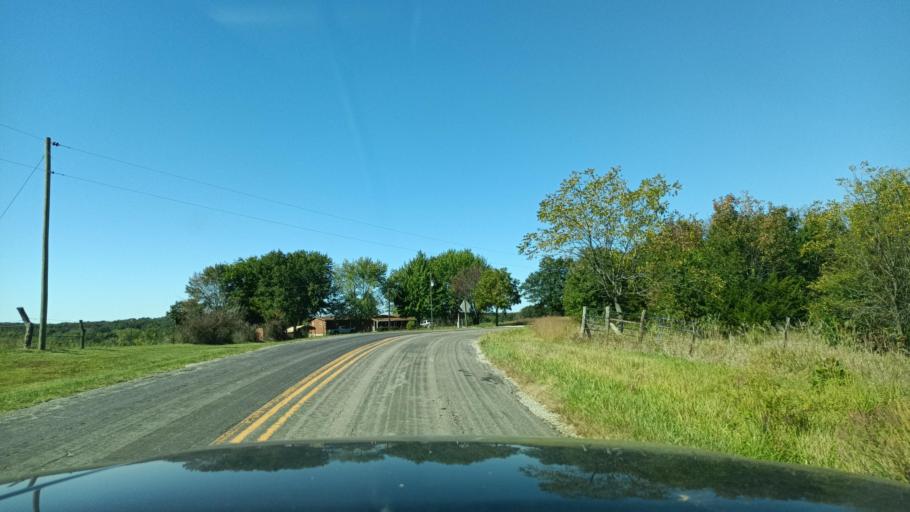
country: US
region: Missouri
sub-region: Scotland County
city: Memphis
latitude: 40.3479
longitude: -92.3303
